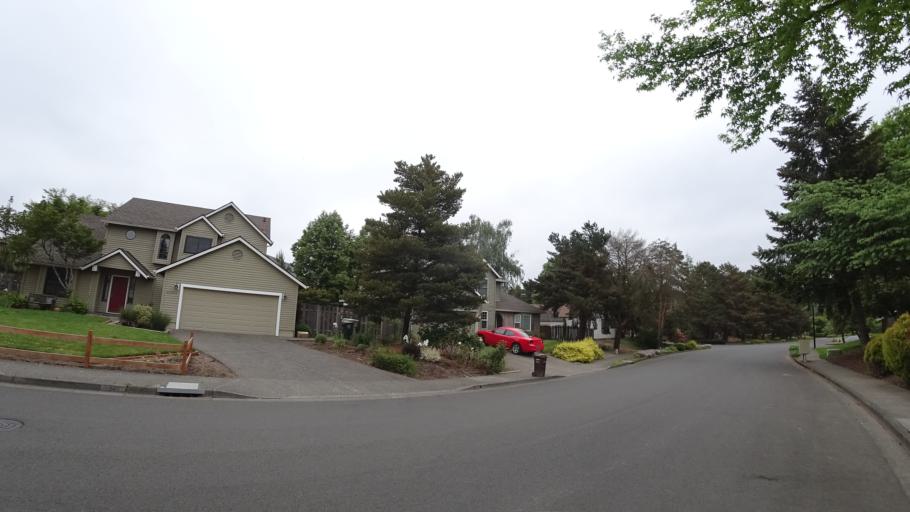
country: US
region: Oregon
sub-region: Washington County
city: Rockcreek
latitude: 45.5593
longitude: -122.8860
